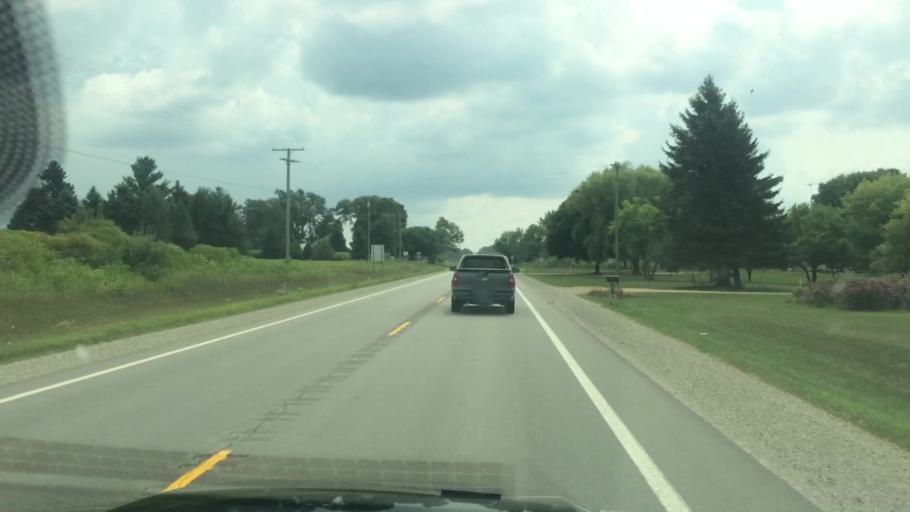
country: US
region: Michigan
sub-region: Tuscola County
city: Cass City
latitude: 43.5757
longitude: -83.0966
